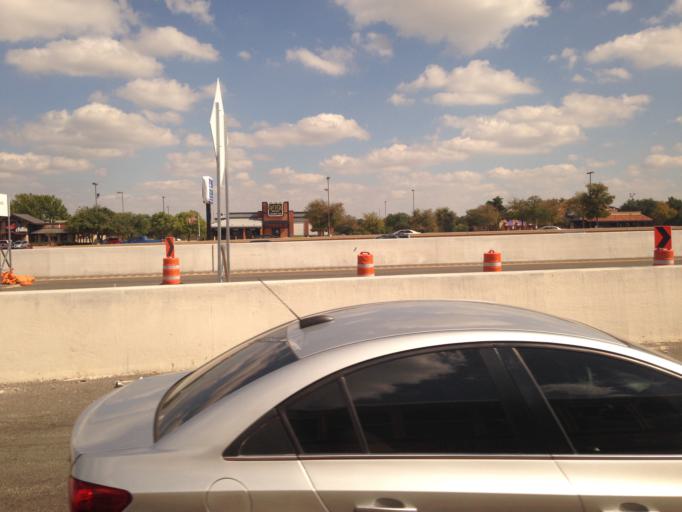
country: US
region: Texas
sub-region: Tarrant County
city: Blue Mound
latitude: 32.8571
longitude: -97.3139
